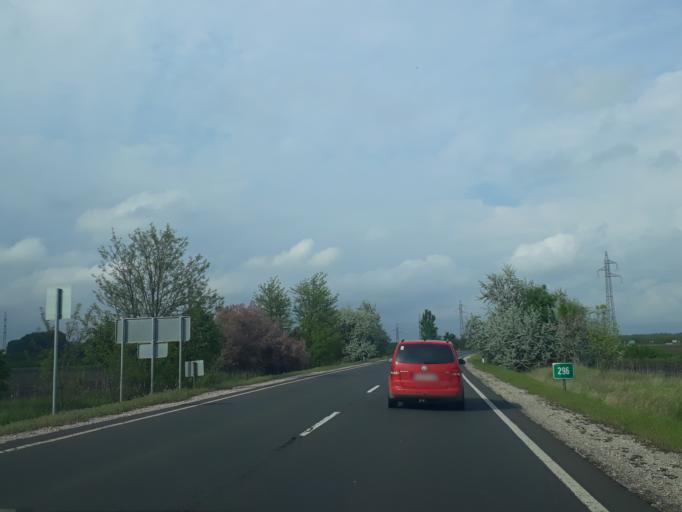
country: HU
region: Szabolcs-Szatmar-Bereg
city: Nyirbogdany
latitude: 48.0634
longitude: 21.9289
